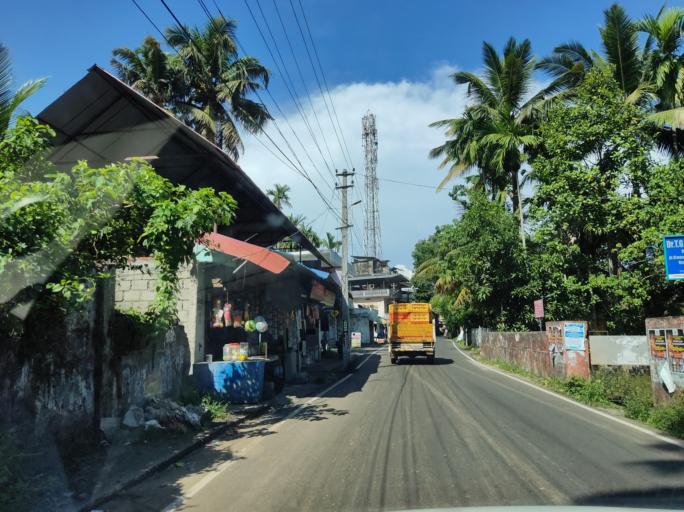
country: IN
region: Kerala
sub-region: Alappuzha
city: Kayankulam
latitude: 9.2588
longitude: 76.4088
